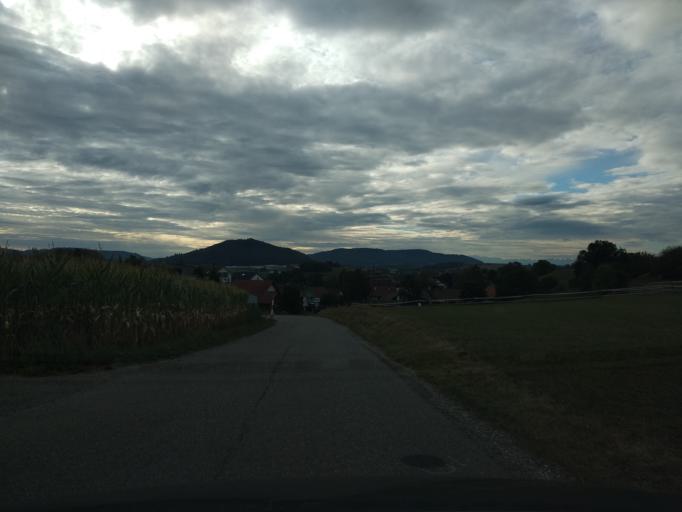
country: CH
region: Thurgau
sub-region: Frauenfeld District
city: Diessenhofen
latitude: 47.6833
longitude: 8.7317
